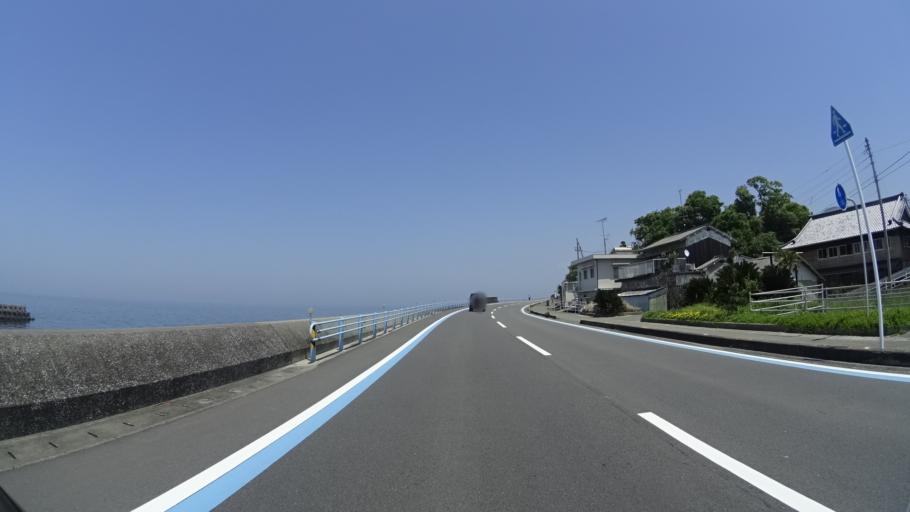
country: JP
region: Ehime
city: Iyo
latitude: 33.6821
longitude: 132.6292
